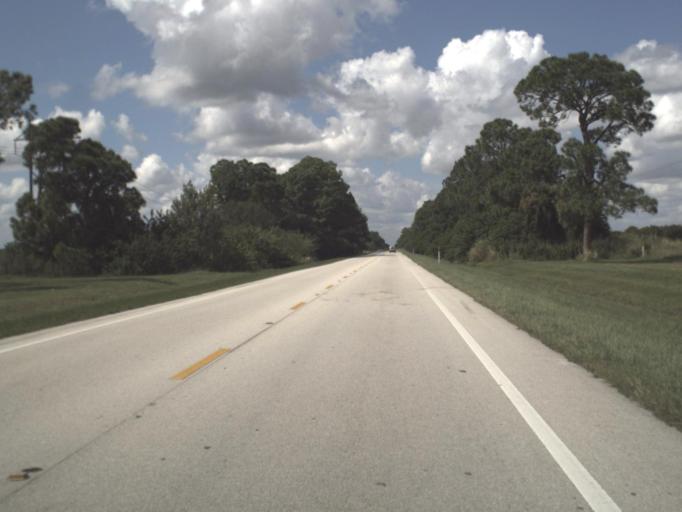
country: US
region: Florida
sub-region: Collier County
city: Immokalee
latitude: 26.5031
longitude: -81.5033
